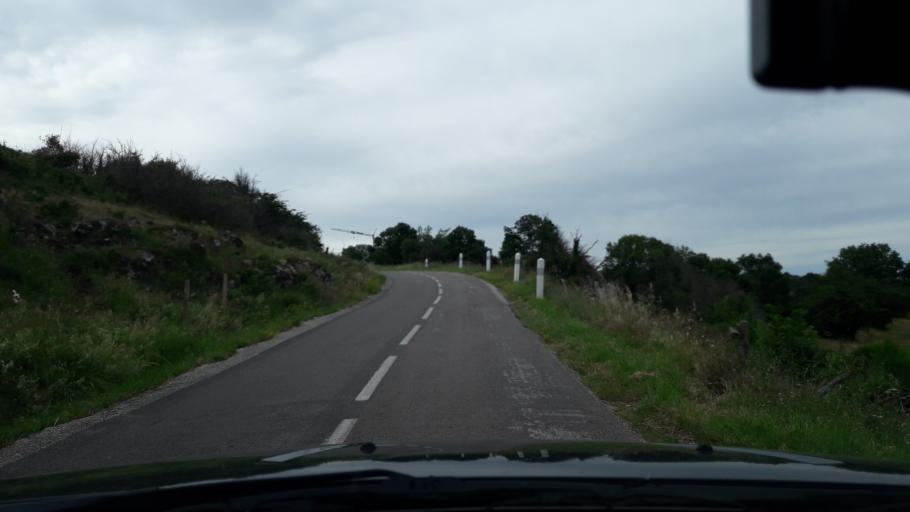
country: FR
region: Rhone-Alpes
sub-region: Departement de l'Ardeche
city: Saint-Priest
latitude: 44.6687
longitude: 4.5610
